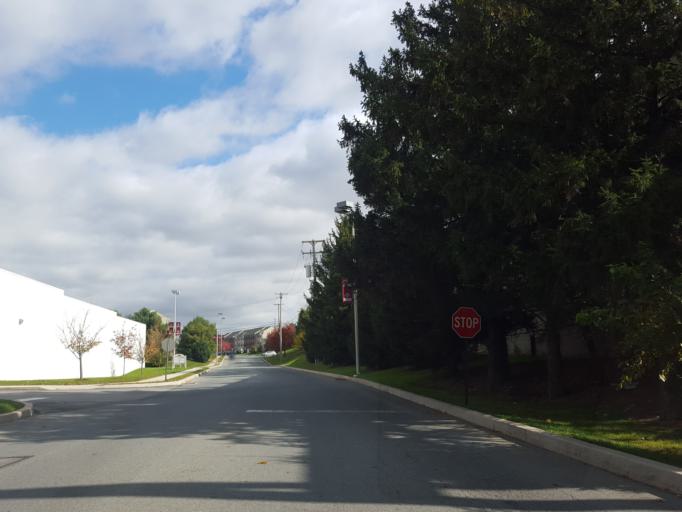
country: US
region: Pennsylvania
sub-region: York County
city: Yoe
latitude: 39.9176
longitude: -76.6283
